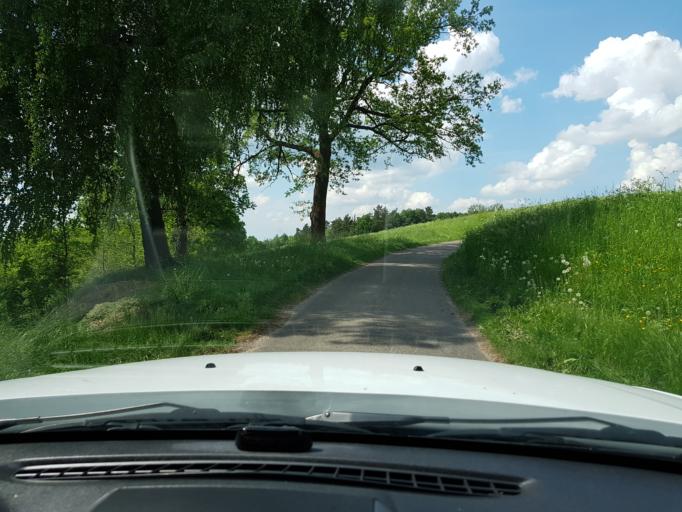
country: PL
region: West Pomeranian Voivodeship
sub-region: Powiat drawski
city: Drawsko Pomorskie
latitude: 53.5194
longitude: 15.7506
